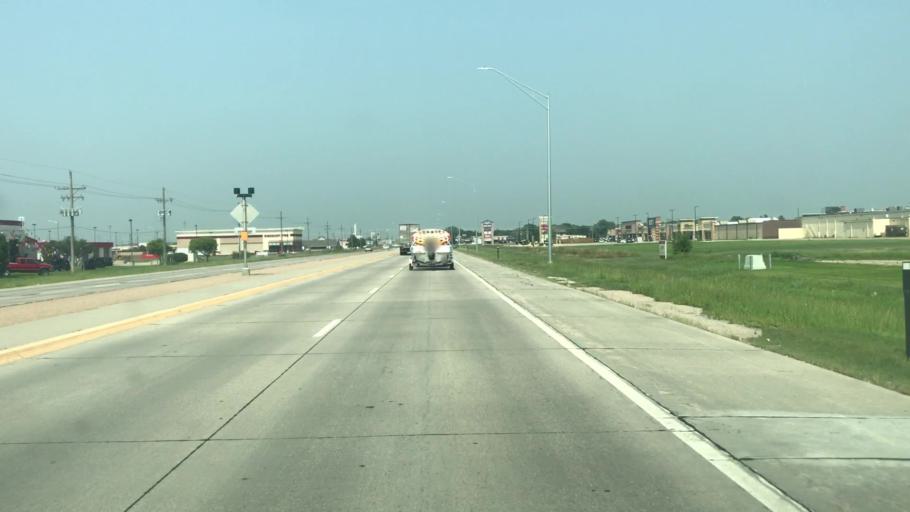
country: US
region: Nebraska
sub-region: Hall County
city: Grand Island
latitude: 40.9399
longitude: -98.3834
